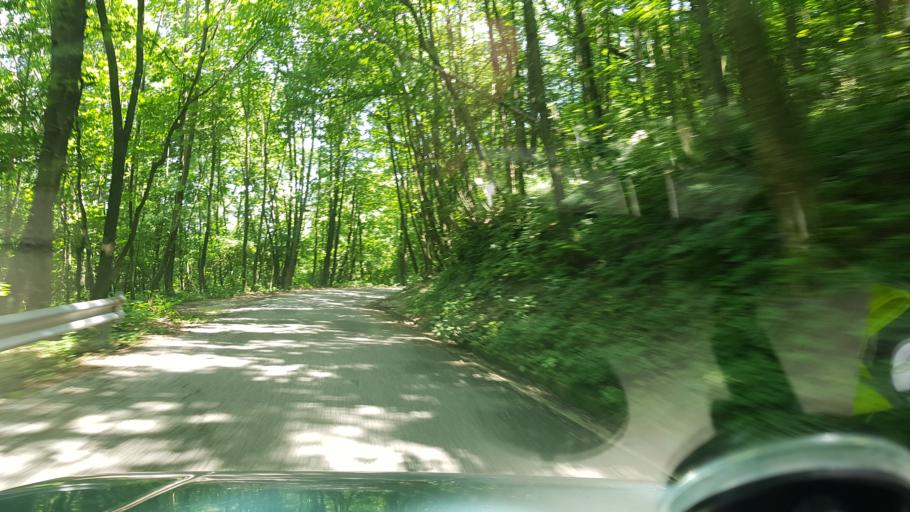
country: IT
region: Friuli Venezia Giulia
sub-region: Provincia di Udine
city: Lusevera
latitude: 46.2459
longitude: 13.2797
